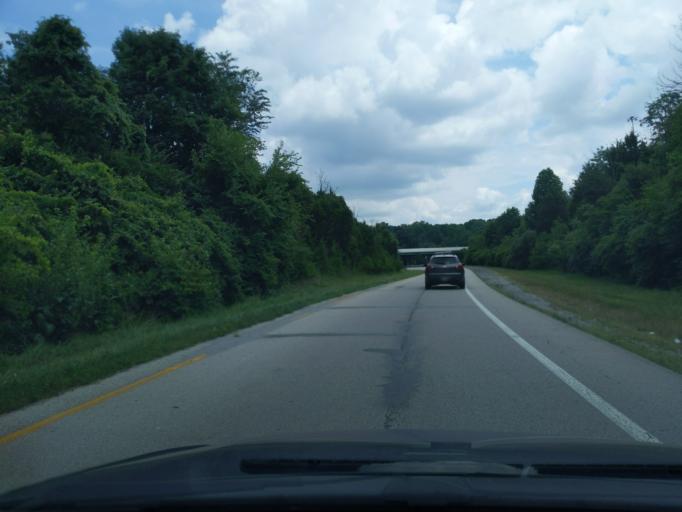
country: US
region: Ohio
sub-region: Hamilton County
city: Highpoint
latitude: 39.2694
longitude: -84.3519
